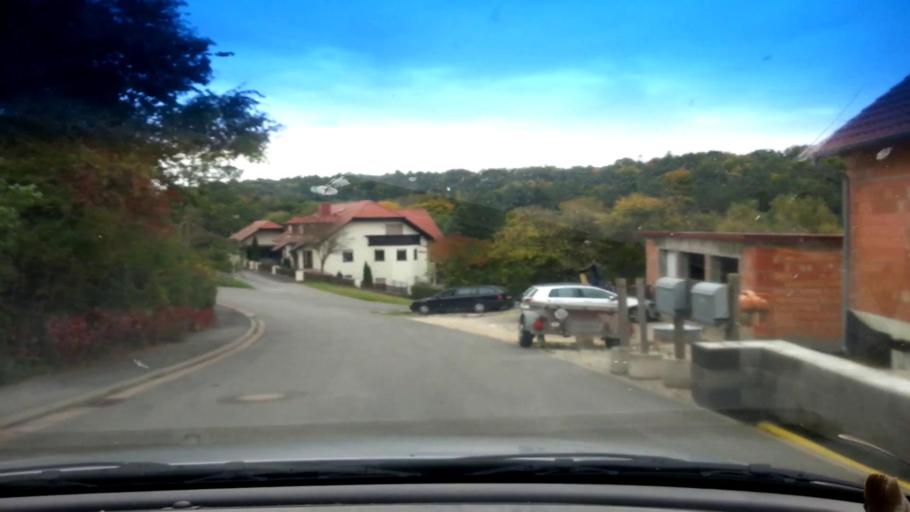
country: DE
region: Bavaria
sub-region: Upper Franconia
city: Priesendorf
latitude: 49.9043
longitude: 10.7178
